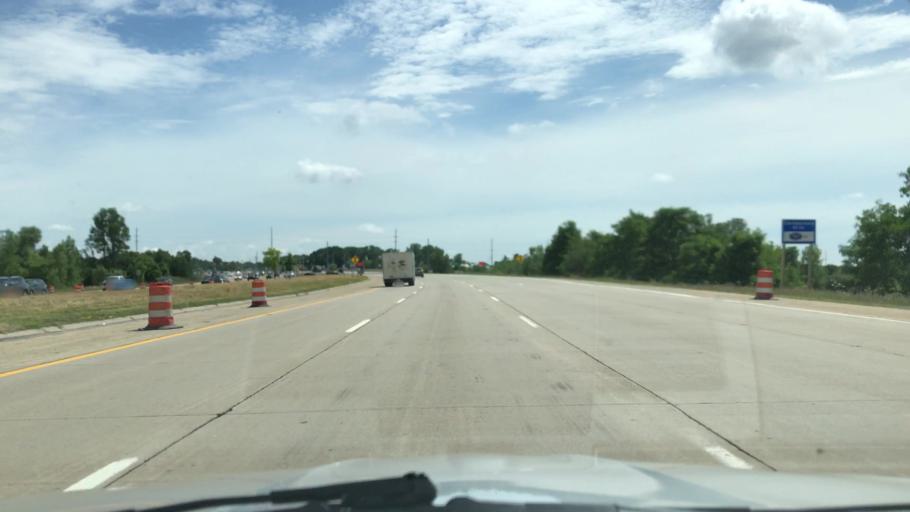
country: US
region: Michigan
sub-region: Oakland County
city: Wolverine Lake
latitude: 42.5457
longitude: -83.4510
